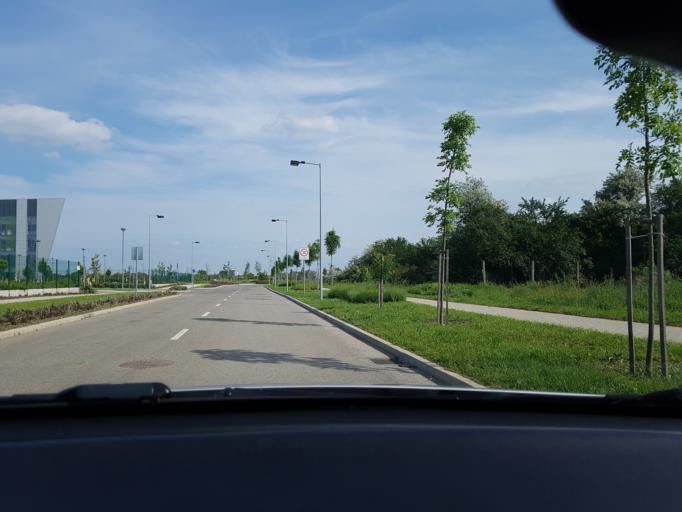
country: HU
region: Csongrad
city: Szeged
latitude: 46.2800
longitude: 20.1024
